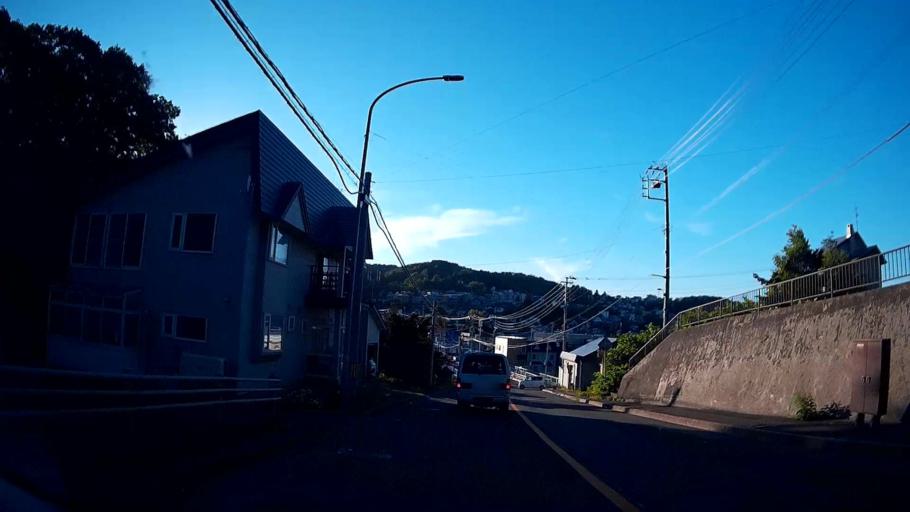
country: JP
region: Hokkaido
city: Otaru
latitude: 43.1681
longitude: 140.9943
